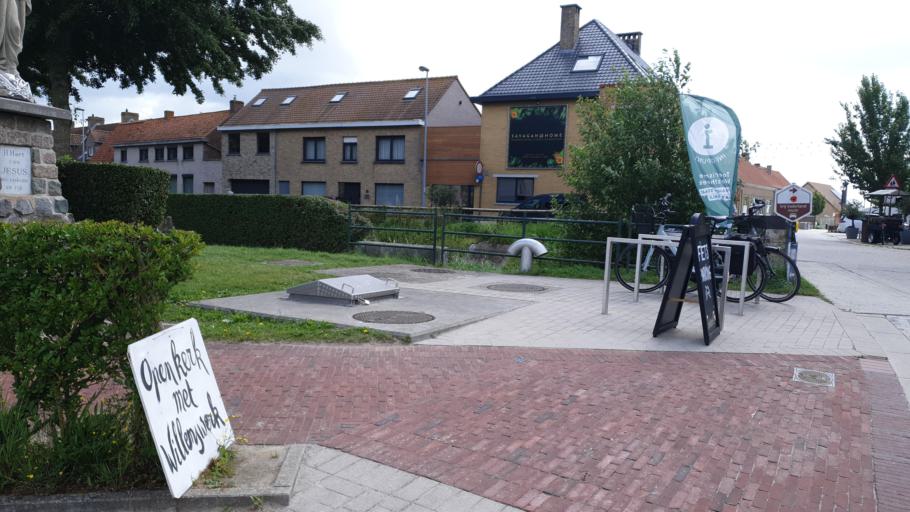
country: BE
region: Flanders
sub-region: Provincie West-Vlaanderen
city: Veurne
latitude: 51.0576
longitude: 2.6889
